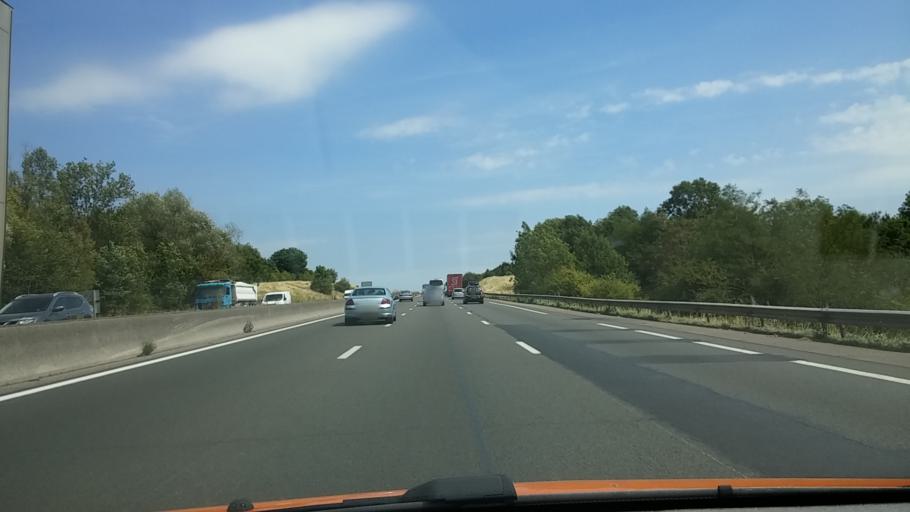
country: FR
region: Ile-de-France
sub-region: Departement de Seine-et-Marne
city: Bussy-Saint-Georges
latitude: 48.8308
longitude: 2.6900
